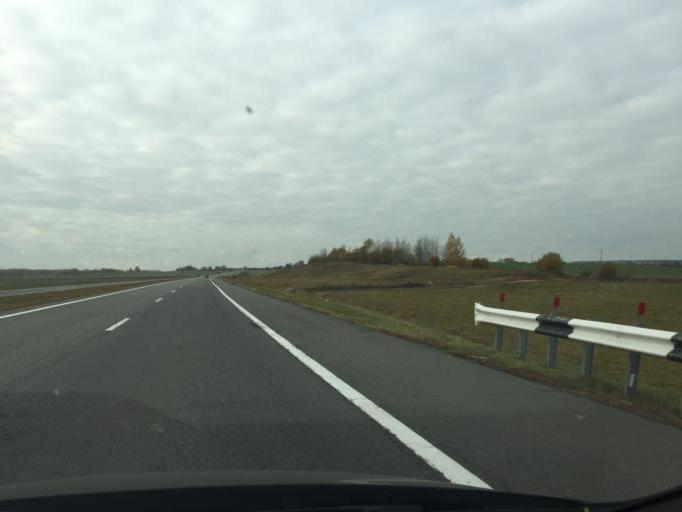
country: BY
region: Minsk
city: Stan'kava
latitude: 53.6757
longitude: 27.2342
